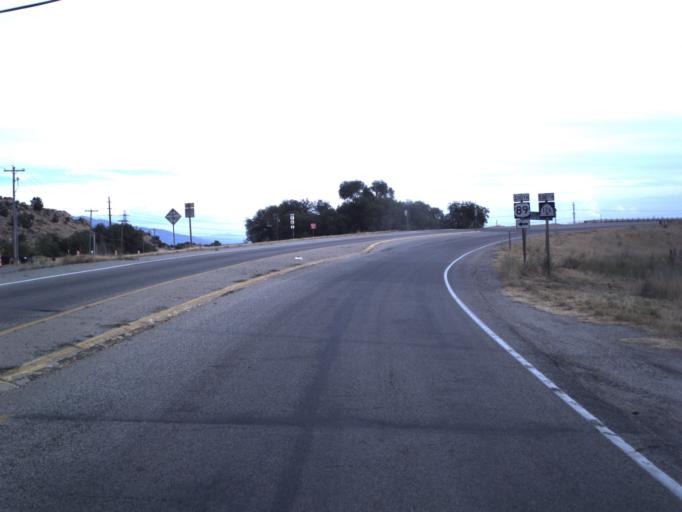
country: US
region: Utah
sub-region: Box Elder County
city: South Willard
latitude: 41.3464
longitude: -112.0334
